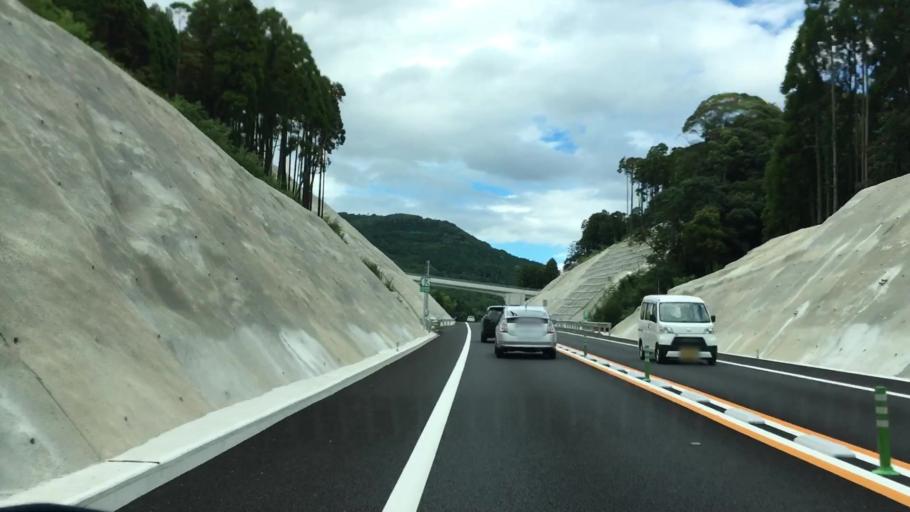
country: JP
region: Saga Prefecture
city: Imaricho-ko
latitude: 33.3044
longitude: 129.9159
